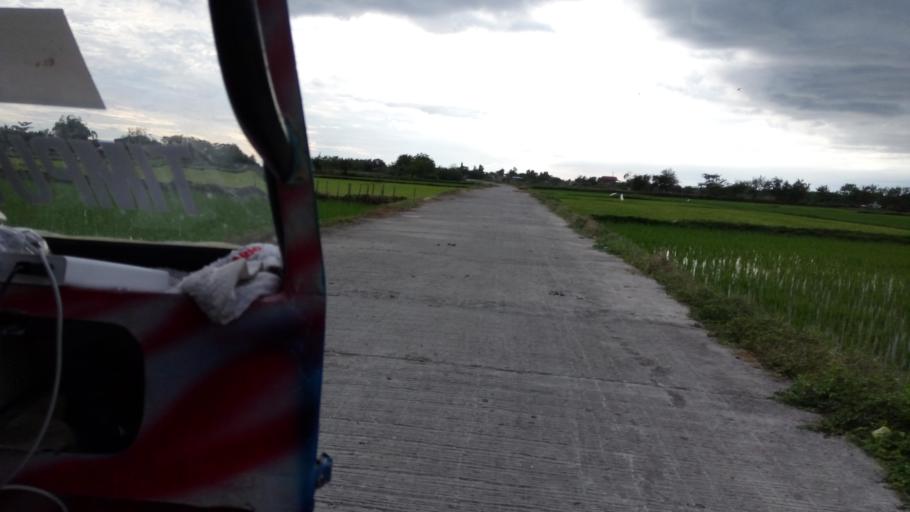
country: PH
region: Ilocos
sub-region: Province of La Union
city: Namboongan
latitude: 16.3020
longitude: 120.3711
